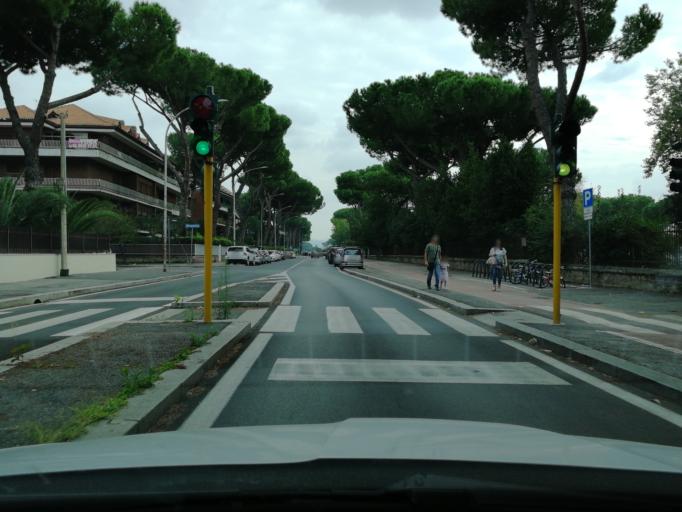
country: IT
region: Latium
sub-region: Citta metropolitana di Roma Capitale
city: Rome
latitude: 41.8508
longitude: 12.5606
